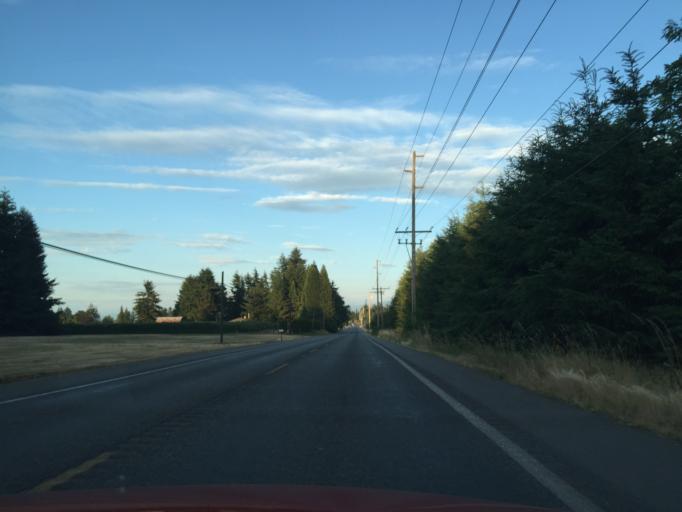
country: US
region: Washington
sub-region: Whatcom County
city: Lynden
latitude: 48.9352
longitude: -122.5231
